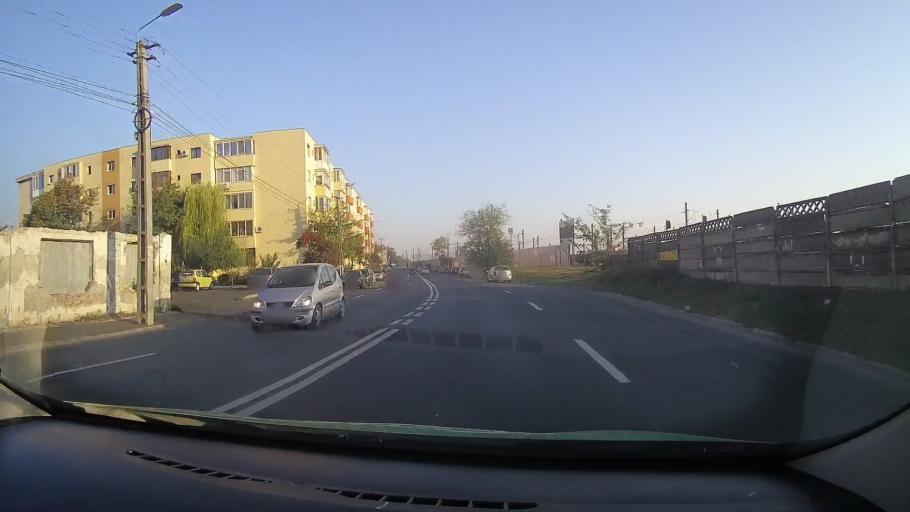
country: RO
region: Arad
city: Arad
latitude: 46.1954
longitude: 21.3206
